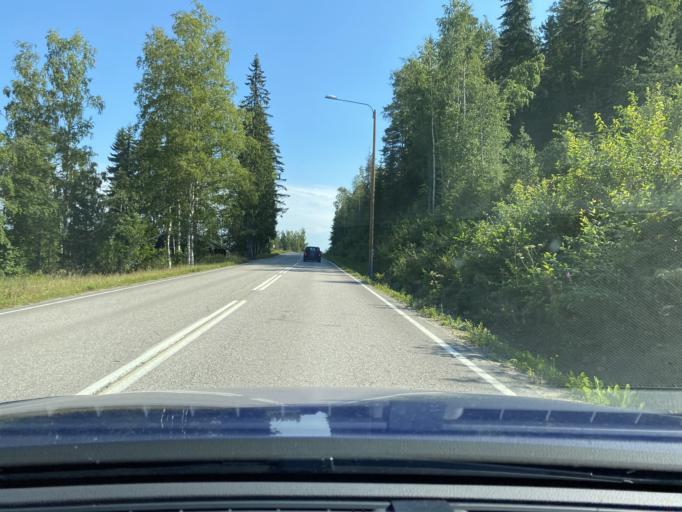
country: FI
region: Central Finland
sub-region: Jaemsae
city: Jaemsae
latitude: 61.8919
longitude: 25.3286
